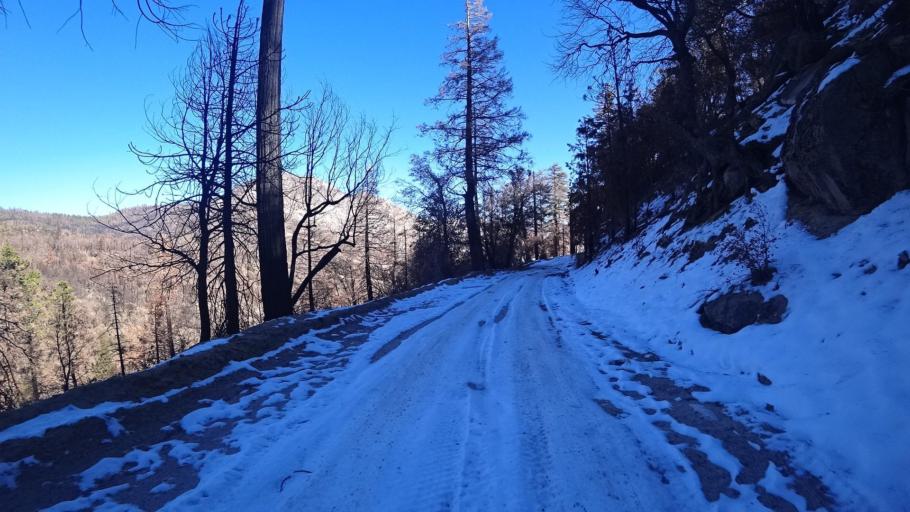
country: US
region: California
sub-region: Kern County
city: Alta Sierra
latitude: 35.7165
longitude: -118.5399
